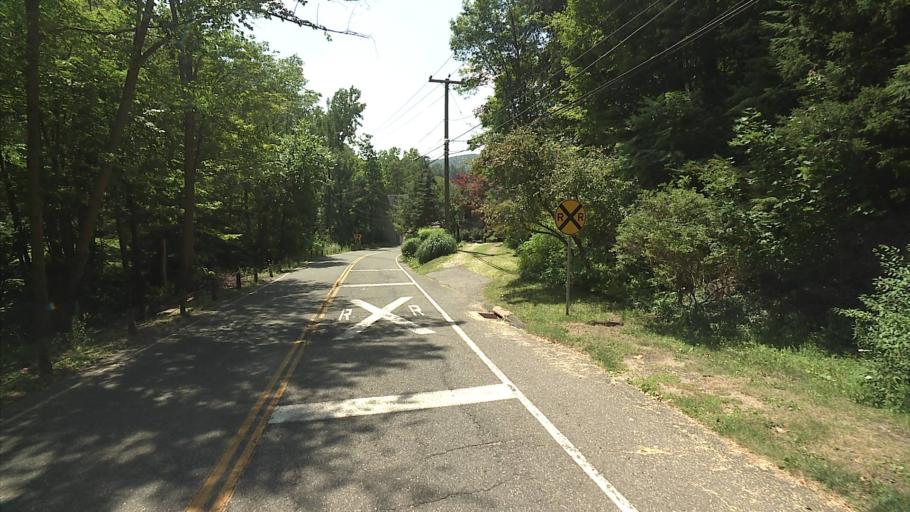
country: US
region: Connecticut
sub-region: Litchfield County
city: Canaan
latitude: 41.8723
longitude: -73.3596
